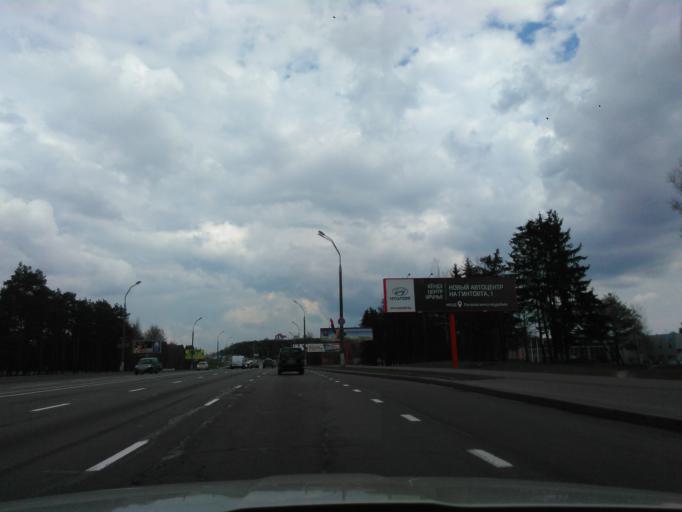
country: BY
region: Minsk
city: Lyeskawka
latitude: 53.9536
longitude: 27.7146
